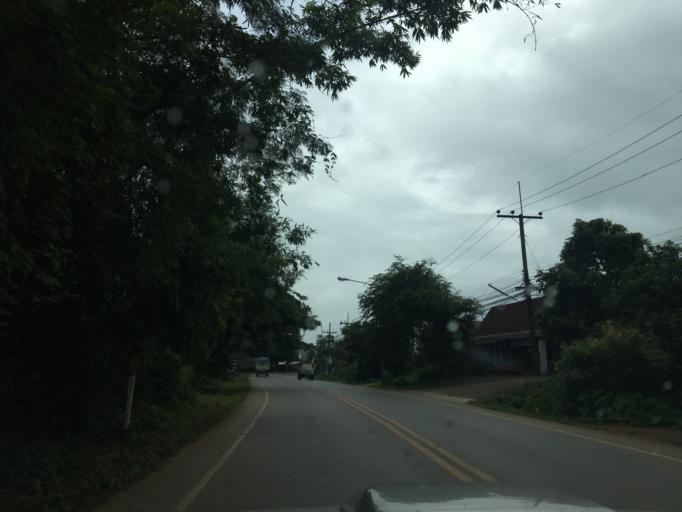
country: TH
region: Chiang Rai
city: Chiang Rai
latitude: 20.0055
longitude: 99.8842
